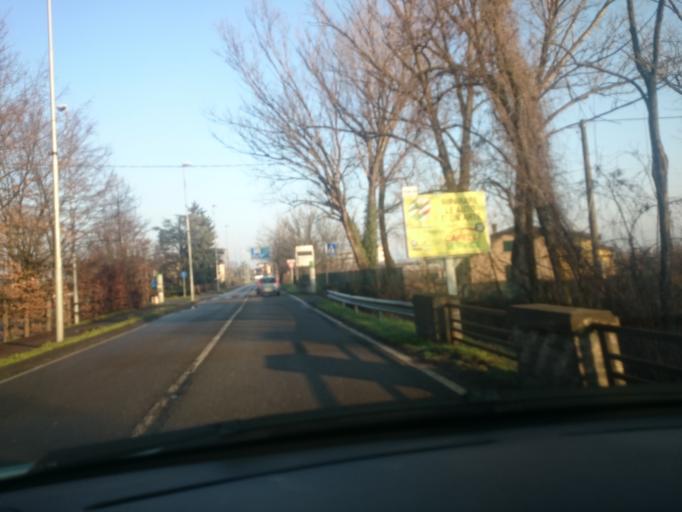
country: IT
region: Emilia-Romagna
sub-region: Provincia di Reggio Emilia
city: Fogliano
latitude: 44.6631
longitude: 10.6447
